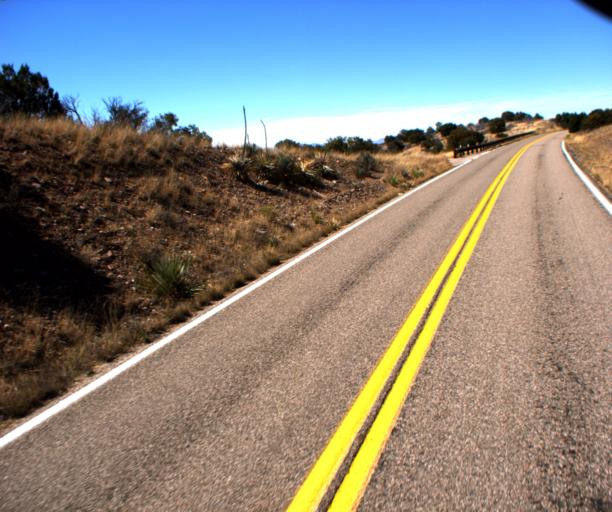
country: US
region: Arizona
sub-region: Cochise County
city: Sierra Vista
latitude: 31.5117
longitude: -110.4966
